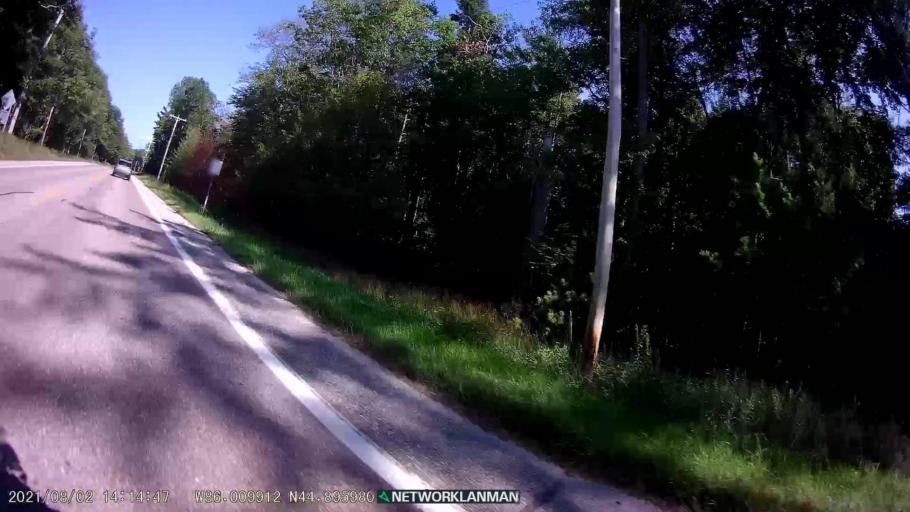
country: US
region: Michigan
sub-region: Benzie County
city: Beulah
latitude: 44.8960
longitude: -86.0096
